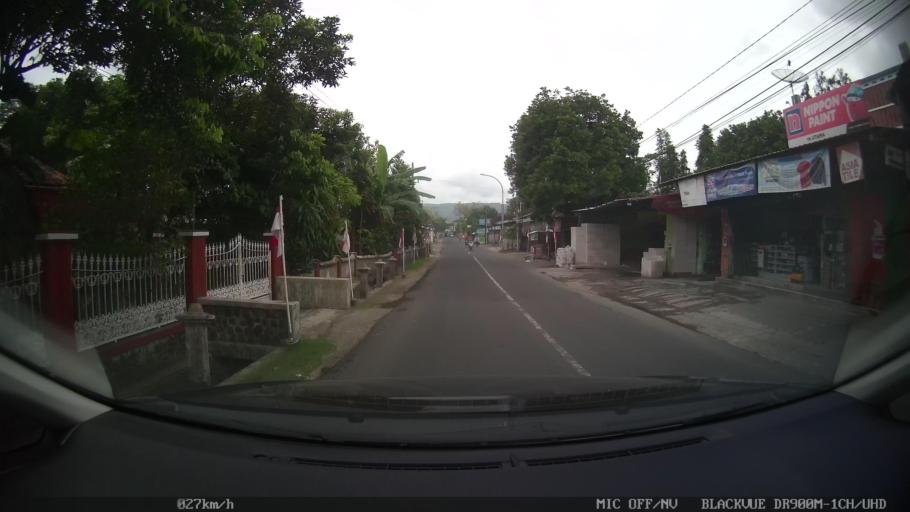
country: ID
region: Daerah Istimewa Yogyakarta
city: Sewon
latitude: -7.8771
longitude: 110.4089
